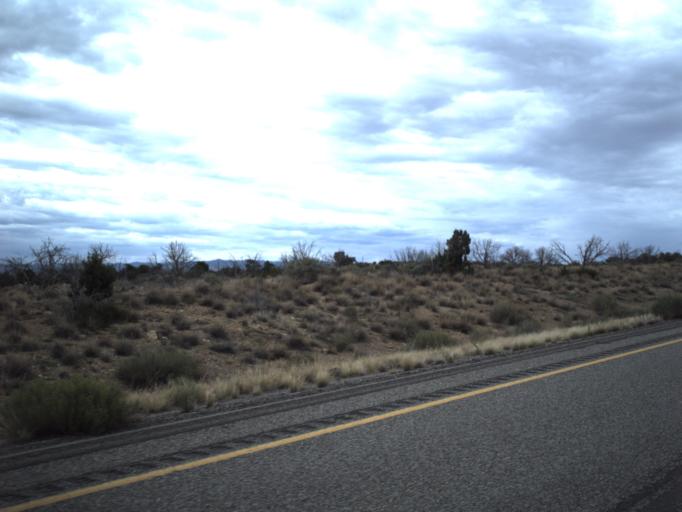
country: US
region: Colorado
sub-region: Mesa County
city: Loma
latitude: 39.1642
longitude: -109.1377
